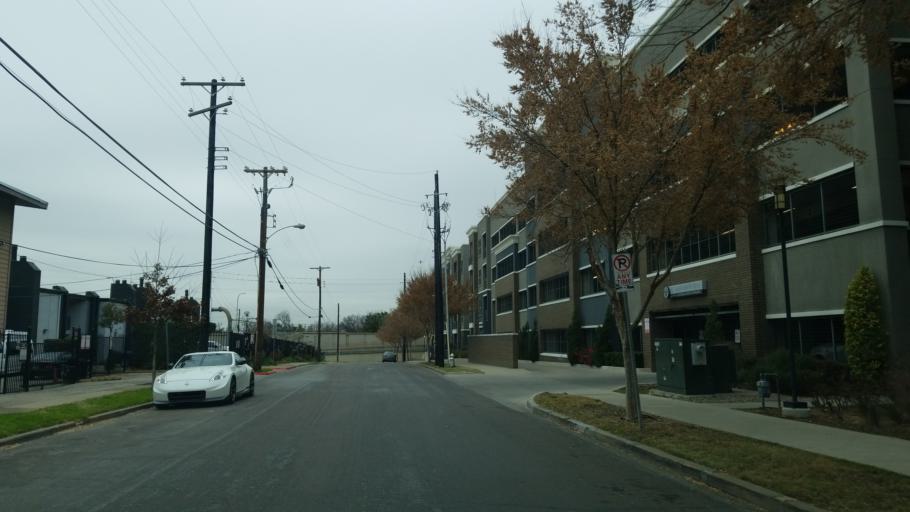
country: US
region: Texas
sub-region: Dallas County
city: Dallas
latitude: 32.8100
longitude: -96.8169
